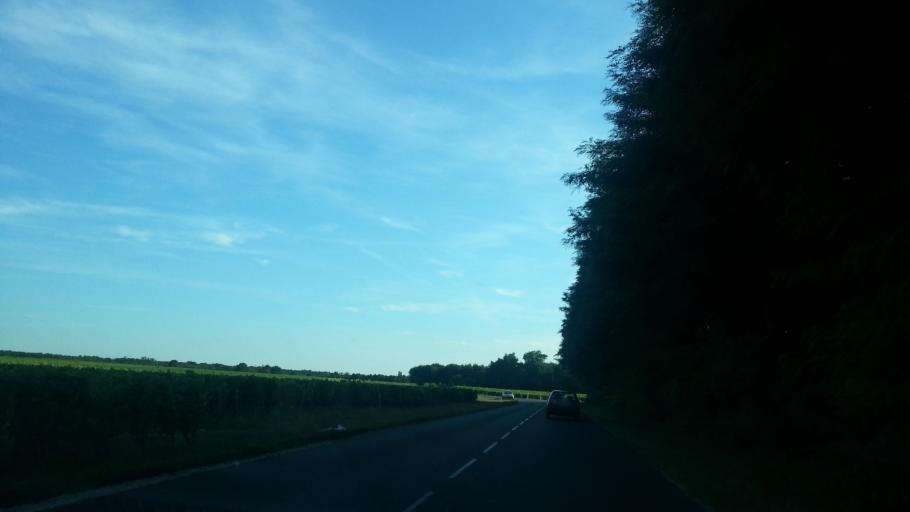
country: FR
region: Aquitaine
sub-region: Departement de la Gironde
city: Podensac
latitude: 44.6328
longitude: -0.3663
